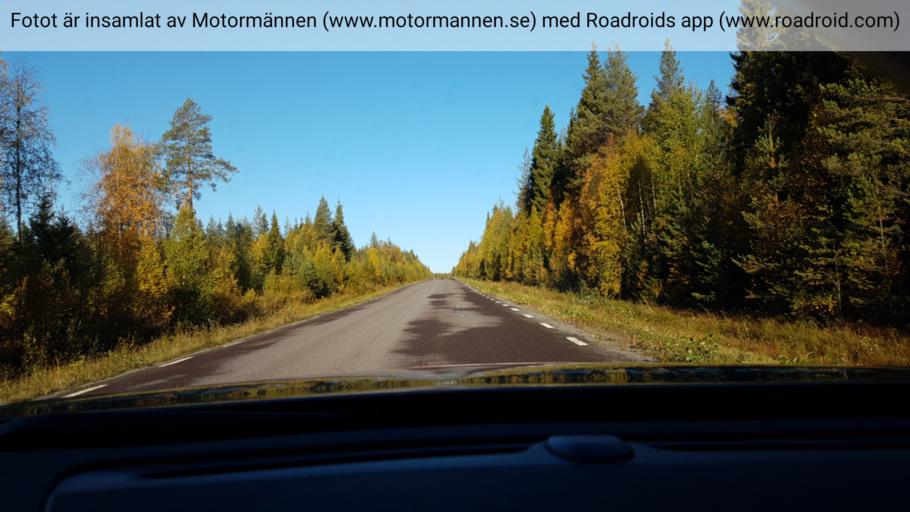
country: SE
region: Norrbotten
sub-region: Bodens Kommun
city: Boden
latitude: 66.0160
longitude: 21.5195
